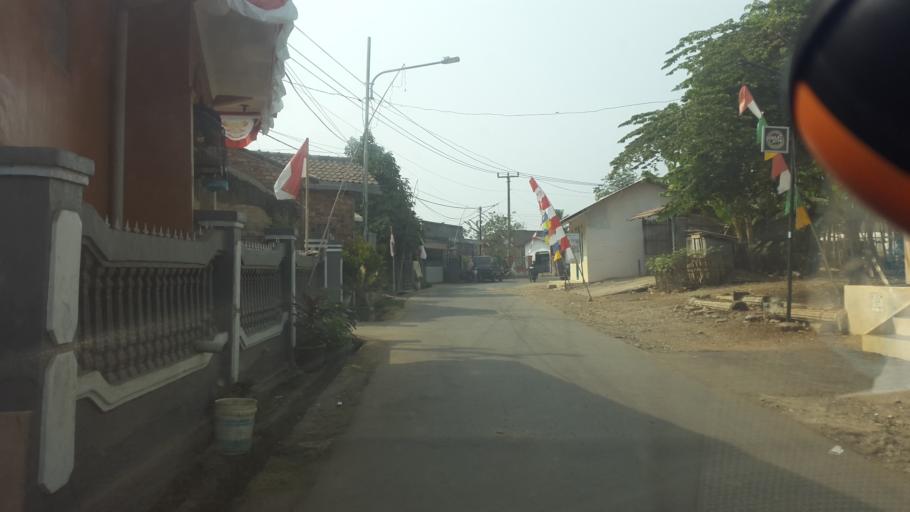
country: ID
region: West Java
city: Cilandak
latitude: -6.9580
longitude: 106.7510
